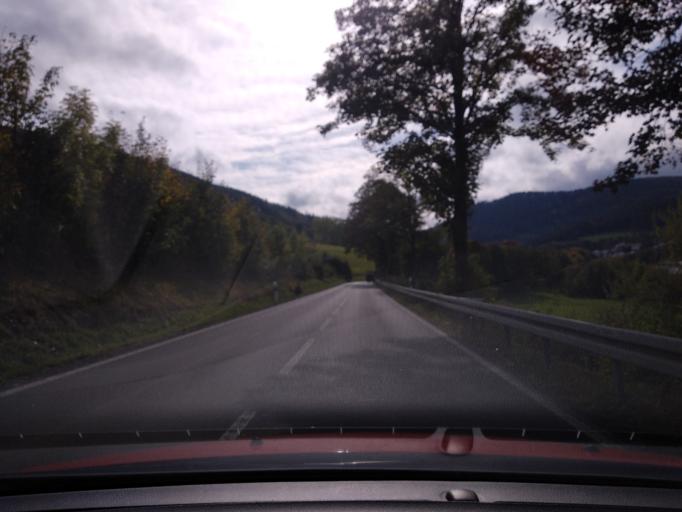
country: DE
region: North Rhine-Westphalia
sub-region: Regierungsbezirk Arnsberg
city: Bestwig
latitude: 51.3241
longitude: 8.4084
